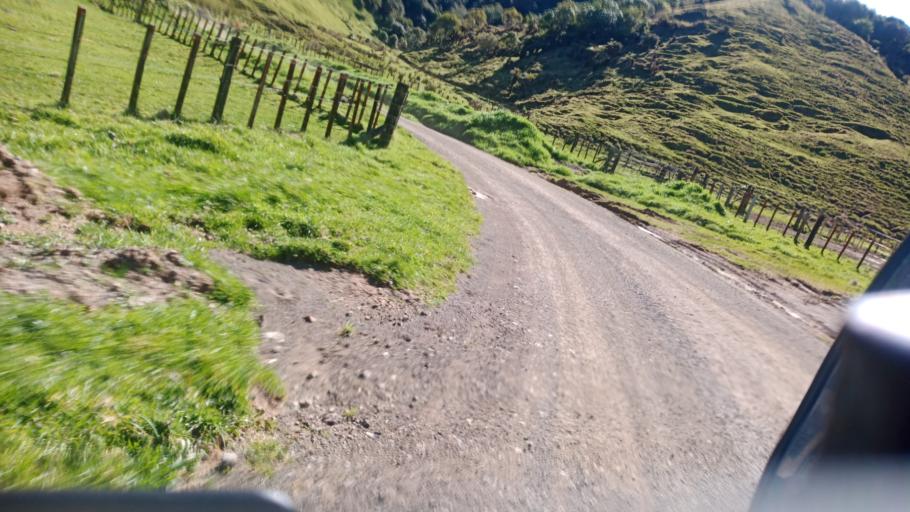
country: NZ
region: Bay of Plenty
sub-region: Opotiki District
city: Opotiki
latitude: -38.1020
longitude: 177.4941
